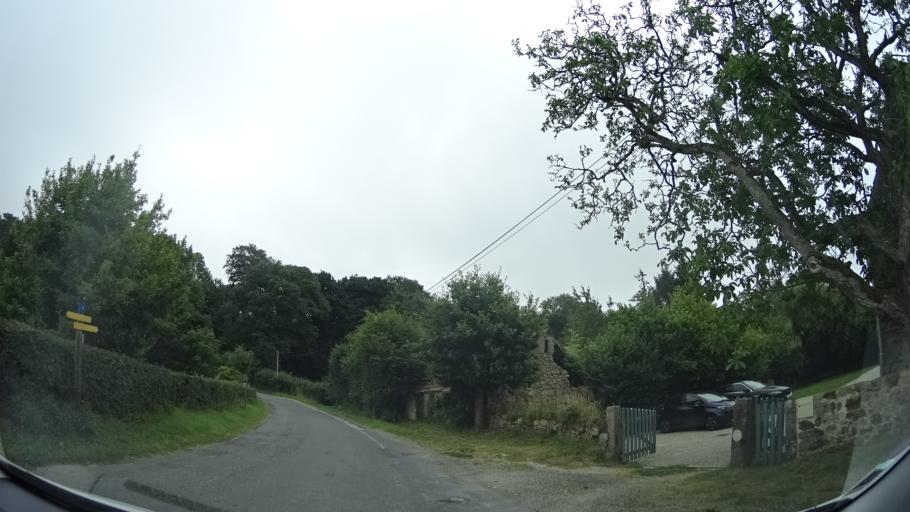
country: FR
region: Lower Normandy
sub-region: Departement de la Manche
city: Les Pieux
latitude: 49.5556
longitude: -1.7477
